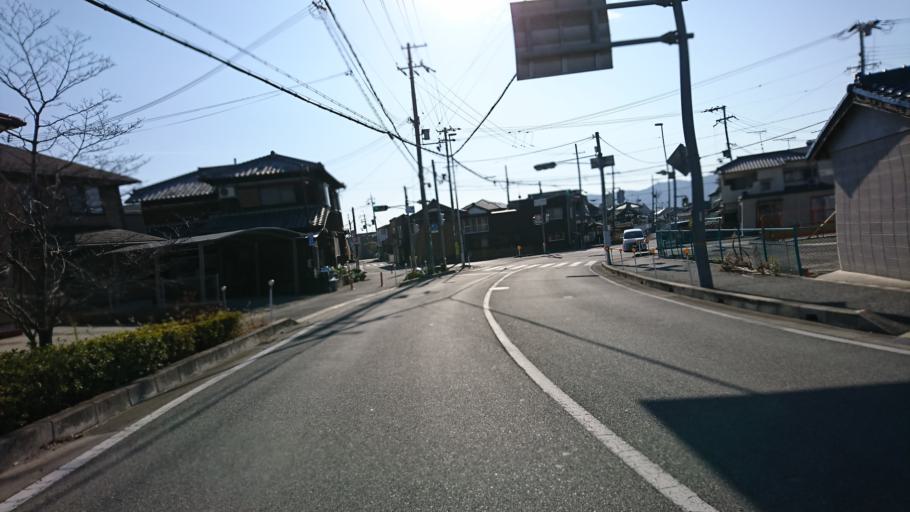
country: JP
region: Hyogo
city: Kakogawacho-honmachi
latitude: 34.8198
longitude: 134.8221
